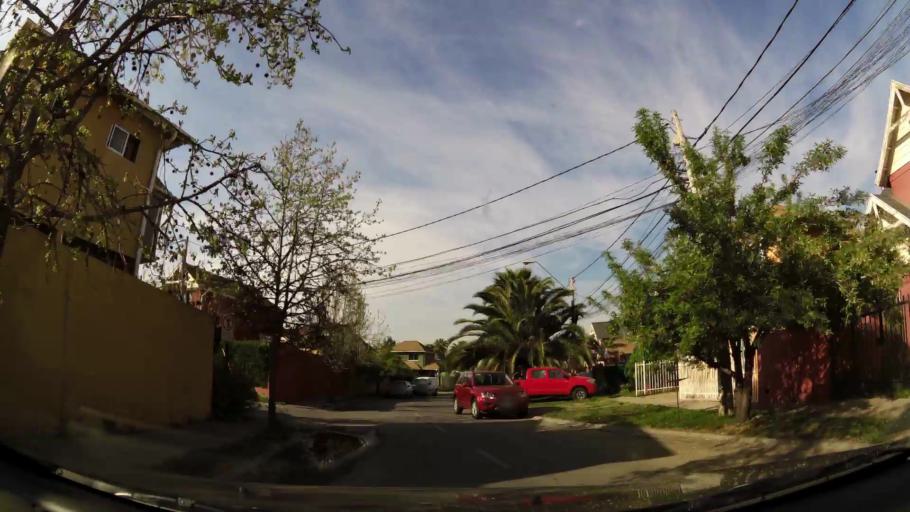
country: CL
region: Santiago Metropolitan
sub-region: Provincia de Cordillera
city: Puente Alto
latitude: -33.5582
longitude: -70.5474
